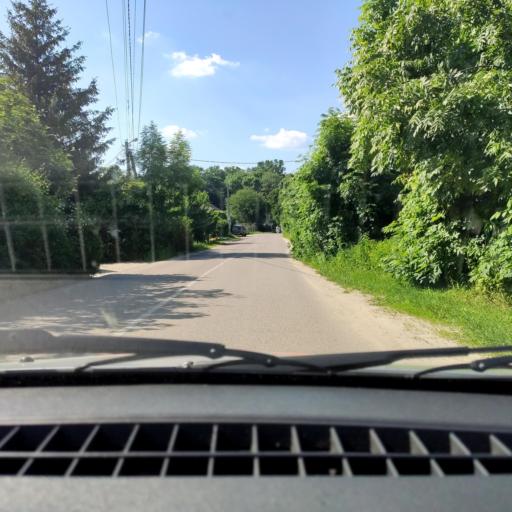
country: RU
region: Voronezj
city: Ramon'
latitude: 51.8190
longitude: 39.2667
